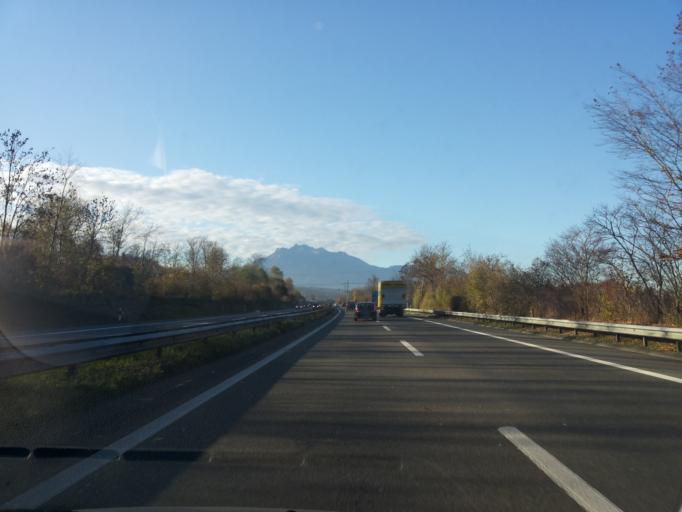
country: CH
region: Lucerne
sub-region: Hochdorf District
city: Inwil
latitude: 47.1130
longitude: 8.3543
